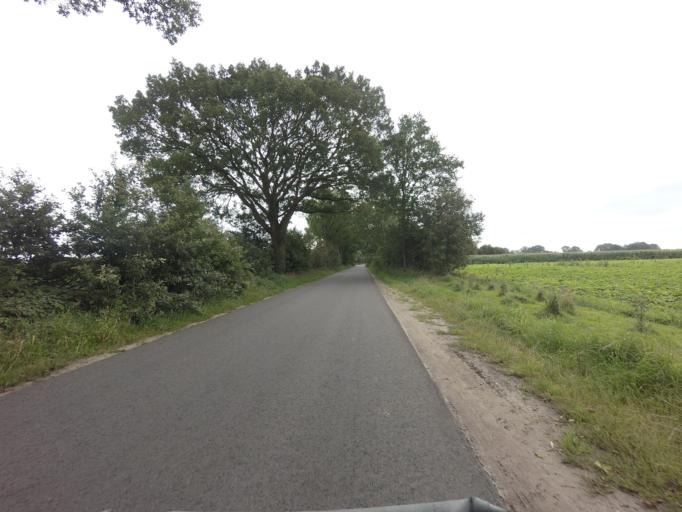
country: NL
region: Overijssel
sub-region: Gemeente Steenwijkerland
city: Steenwijkerwold
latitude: 52.8096
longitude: 6.0310
